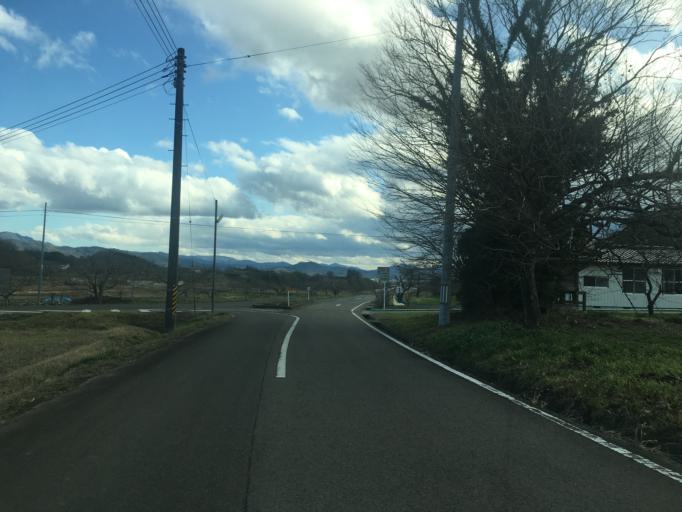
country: JP
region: Fukushima
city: Yanagawamachi-saiwaicho
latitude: 37.8862
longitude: 140.6007
